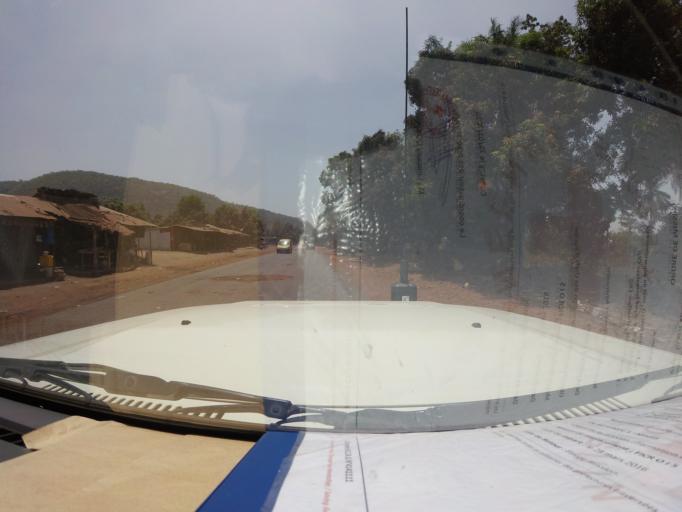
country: GN
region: Kindia
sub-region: Coyah
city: Coyah
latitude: 9.7859
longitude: -13.3152
